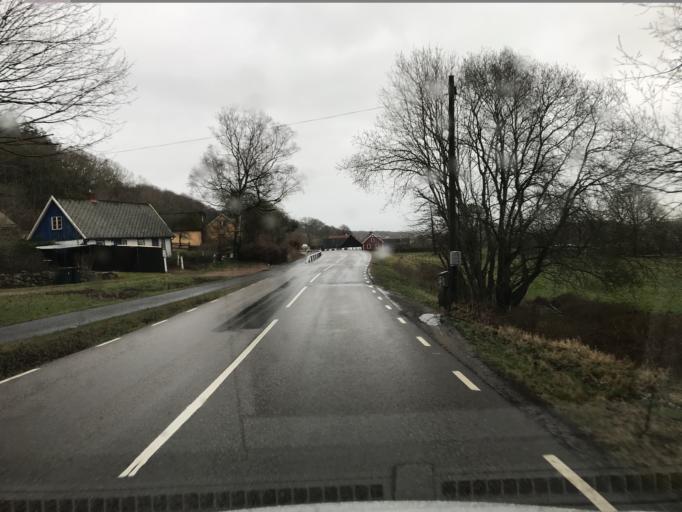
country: SE
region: Skane
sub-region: Bastads Kommun
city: Forslov
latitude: 56.3479
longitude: 12.8561
